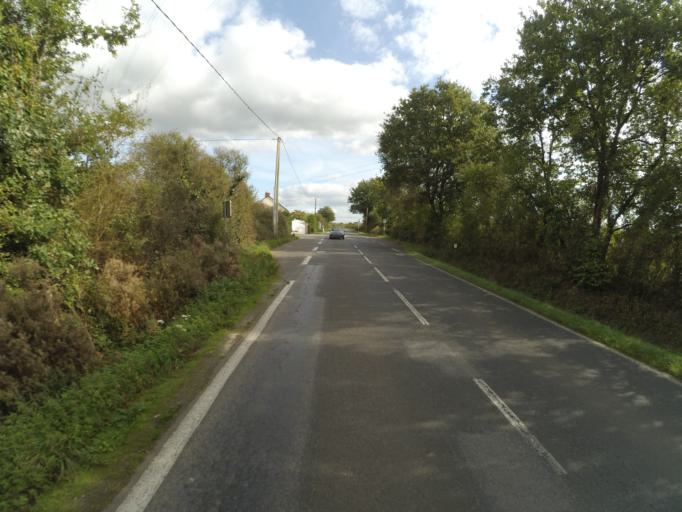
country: FR
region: Pays de la Loire
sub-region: Departement de la Loire-Atlantique
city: Fay-de-Bretagne
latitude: 47.4095
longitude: -1.7603
